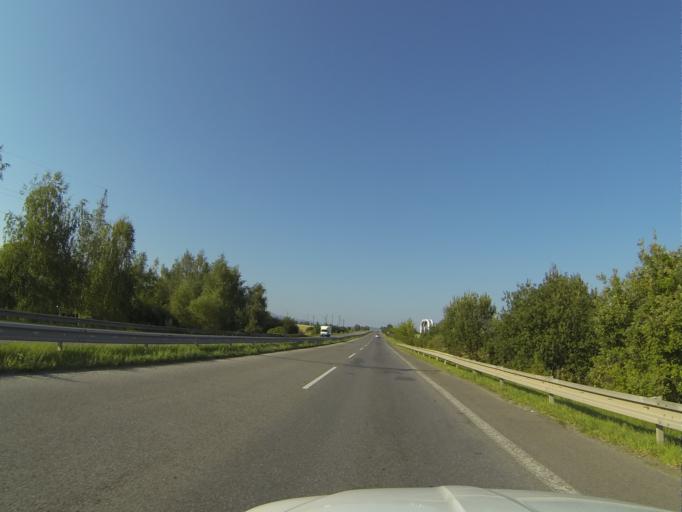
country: SK
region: Nitriansky
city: Prievidza
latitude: 48.7462
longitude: 18.6227
